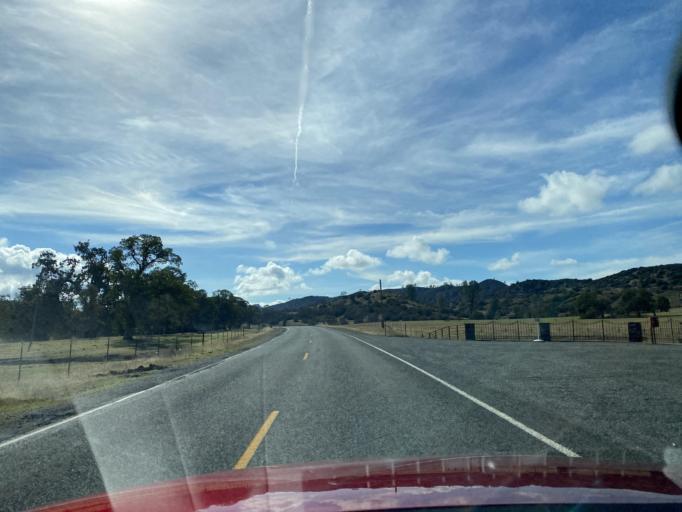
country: US
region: California
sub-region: Glenn County
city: Willows
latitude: 39.4560
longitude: -122.5141
